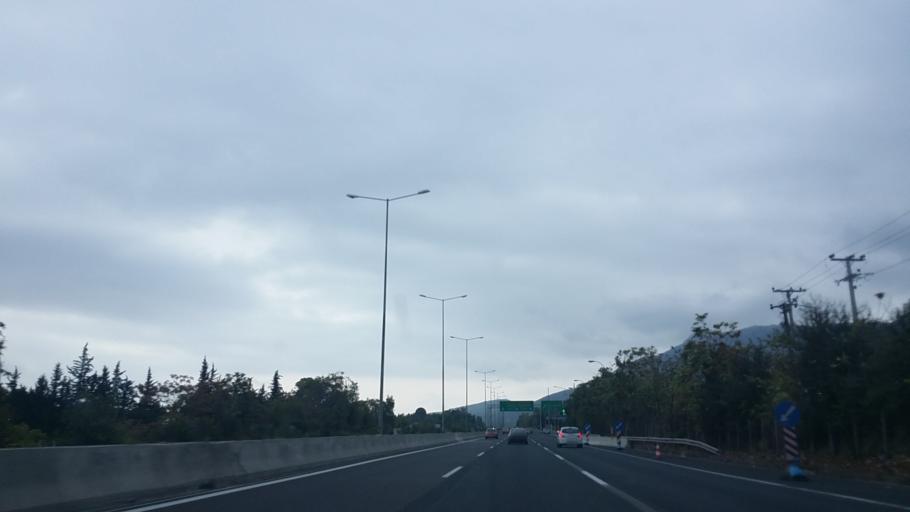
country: GR
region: Attica
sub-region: Nomarchia Anatolikis Attikis
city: Oropos
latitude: 38.2389
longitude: 23.7769
